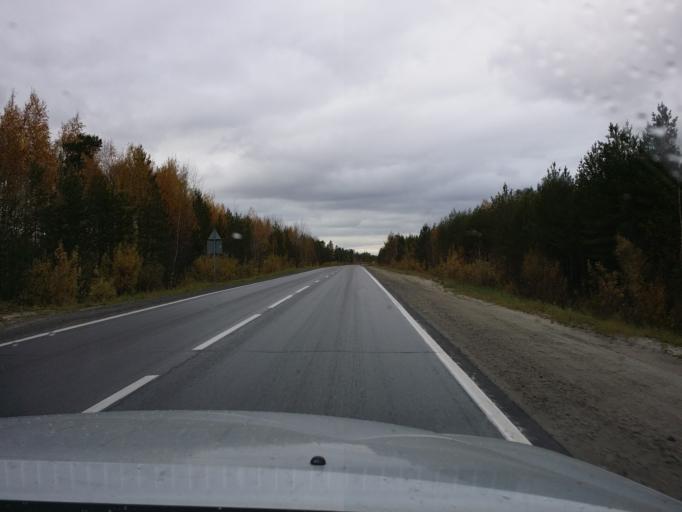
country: RU
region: Khanty-Mansiyskiy Avtonomnyy Okrug
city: Megion
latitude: 61.1078
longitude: 75.8488
